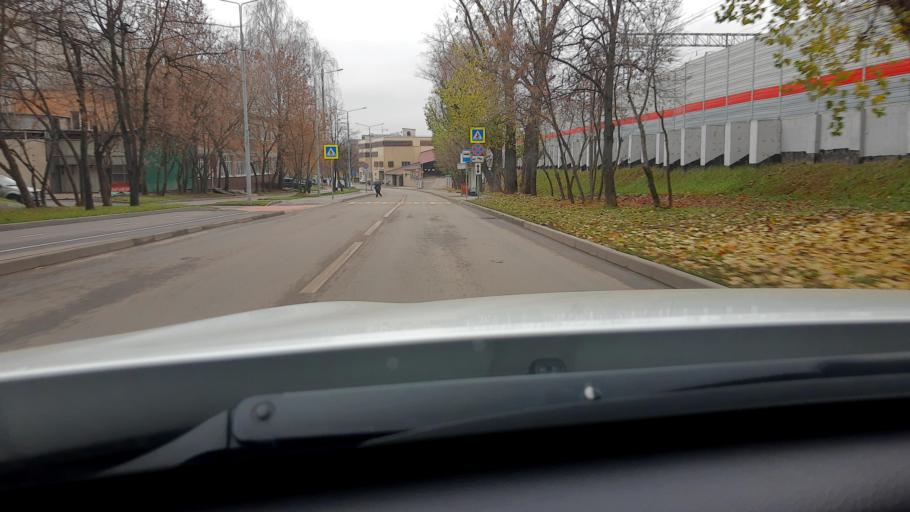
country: RU
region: Moskovskaya
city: Marfino
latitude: 55.7214
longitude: 37.3872
